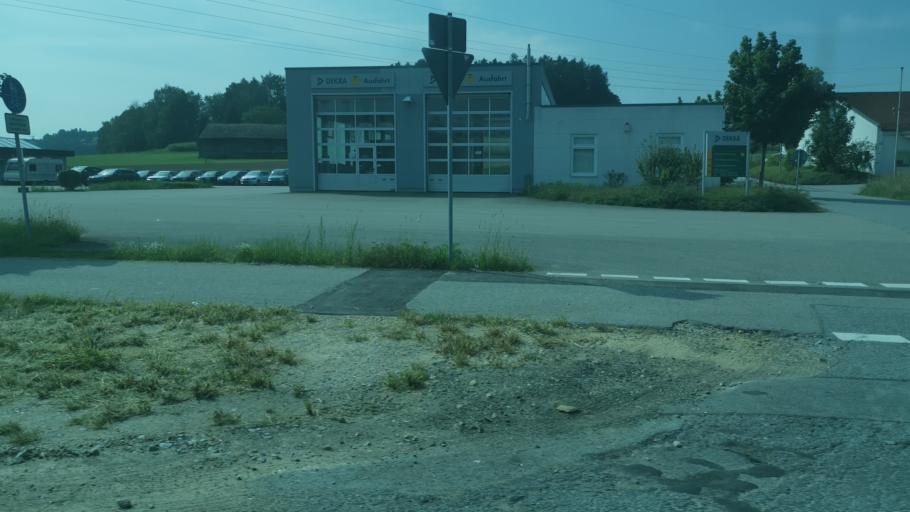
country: DE
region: Bavaria
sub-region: Upper Palatinate
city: Chamerau
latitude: 49.2031
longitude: 12.7411
